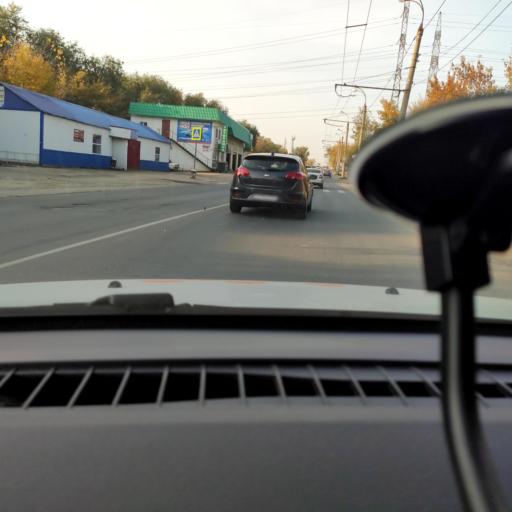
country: RU
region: Samara
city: Petra-Dubrava
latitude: 53.2513
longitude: 50.2679
